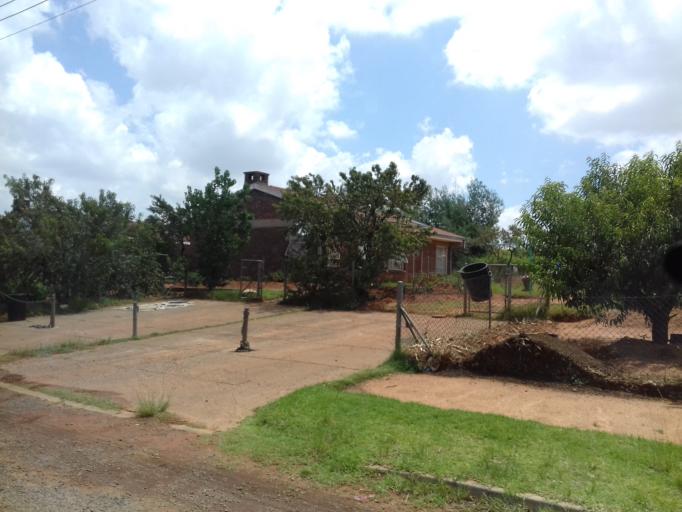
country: LS
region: Maseru
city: Maseru
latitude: -29.4527
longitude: 27.5623
